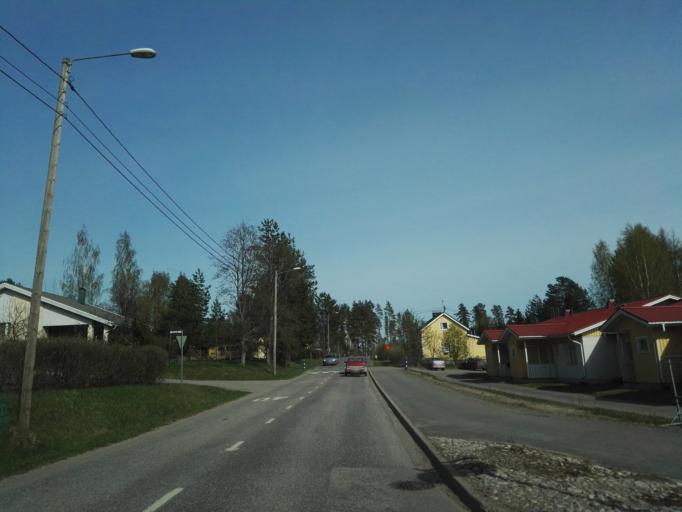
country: FI
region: Central Finland
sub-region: Joutsa
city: Joutsa
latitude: 61.7467
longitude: 26.1317
